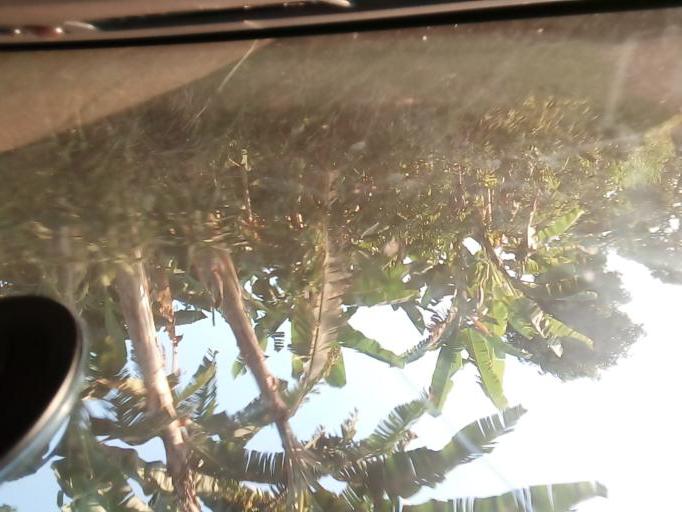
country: UG
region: Central Region
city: Masaka
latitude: -0.3307
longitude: 31.7542
